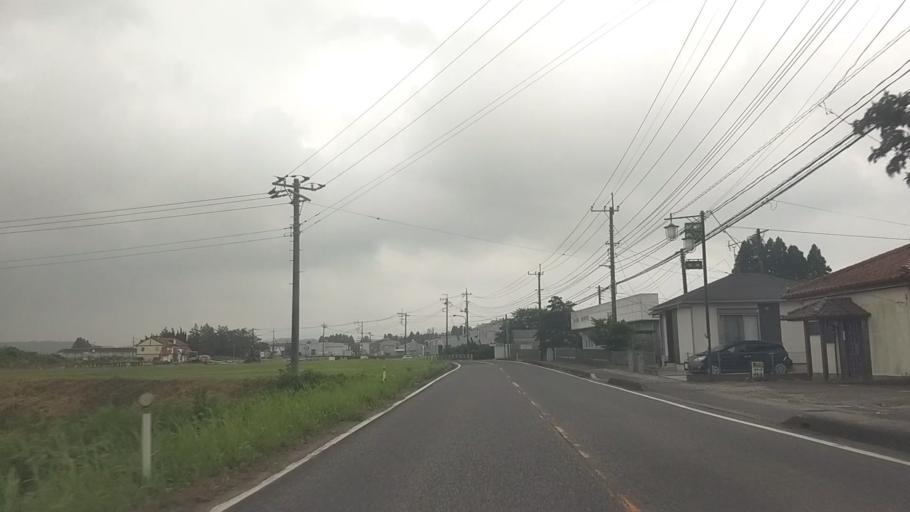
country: JP
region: Chiba
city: Ohara
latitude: 35.2812
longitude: 140.2967
